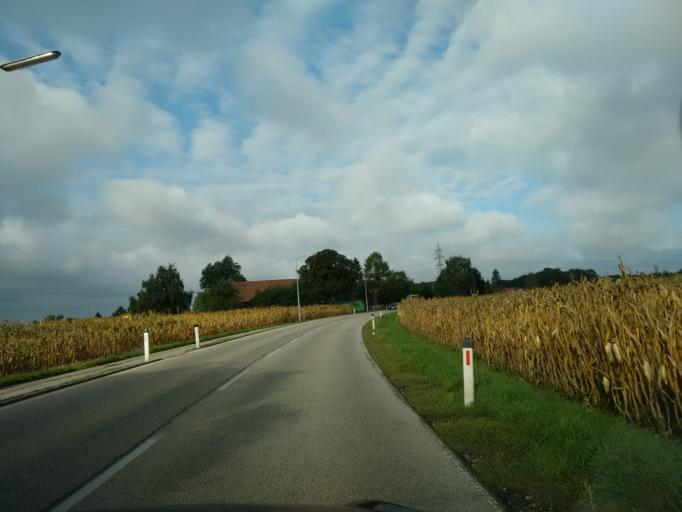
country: AT
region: Upper Austria
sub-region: Politischer Bezirk Linz-Land
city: Traun
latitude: 48.2152
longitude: 14.2170
